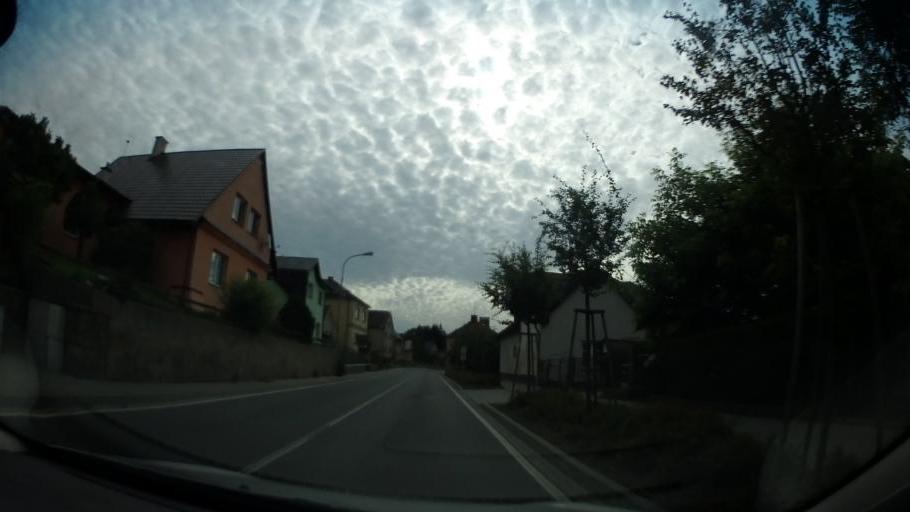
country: CZ
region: Olomoucky
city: Zabreh
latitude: 49.8861
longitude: 16.8688
